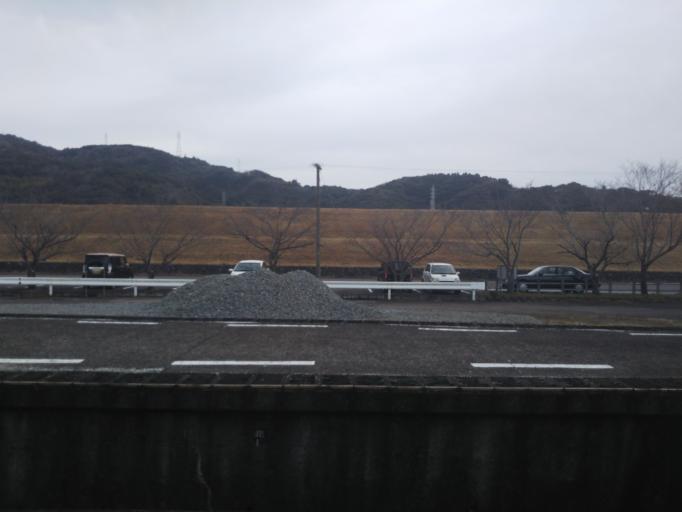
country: JP
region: Kochi
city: Nakamura
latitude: 32.9840
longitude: 132.9445
